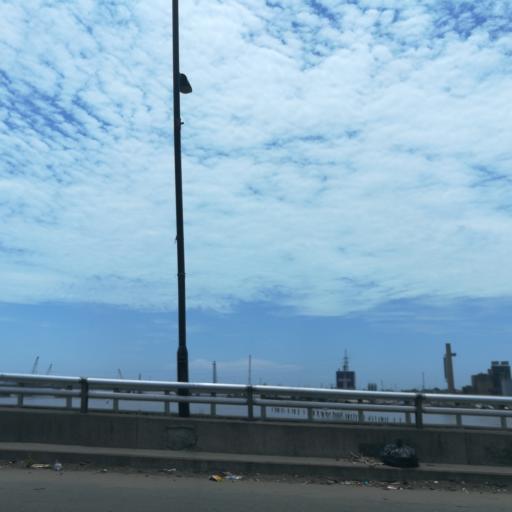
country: NG
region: Lagos
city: Ebute Metta
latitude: 6.4685
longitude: 3.3844
